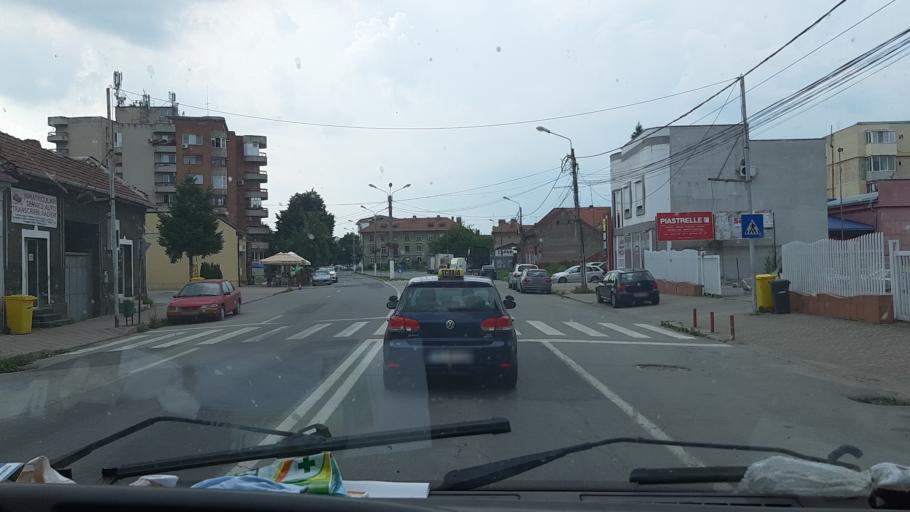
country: RO
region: Timis
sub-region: Municipiul Lugoj
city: Lugoj
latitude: 45.6964
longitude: 21.8996
